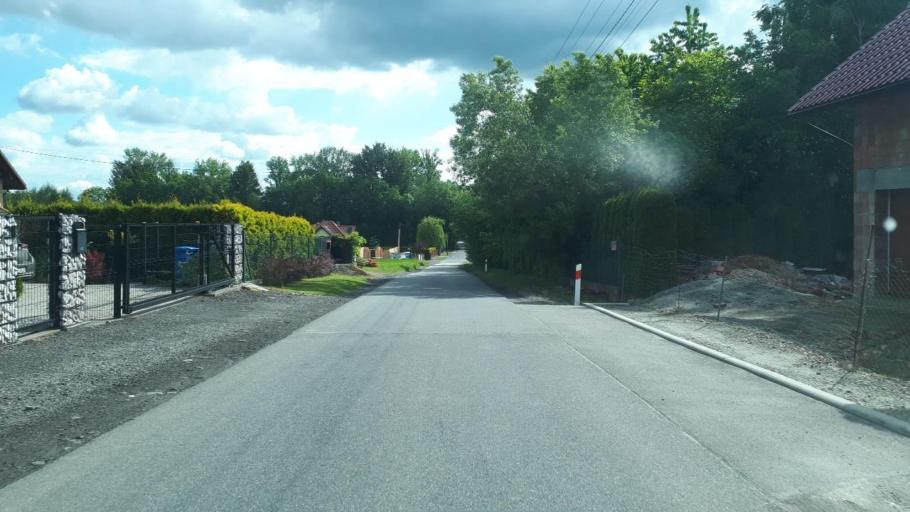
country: PL
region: Silesian Voivodeship
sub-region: Powiat bielski
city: Kozy
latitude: 49.8571
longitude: 19.1207
